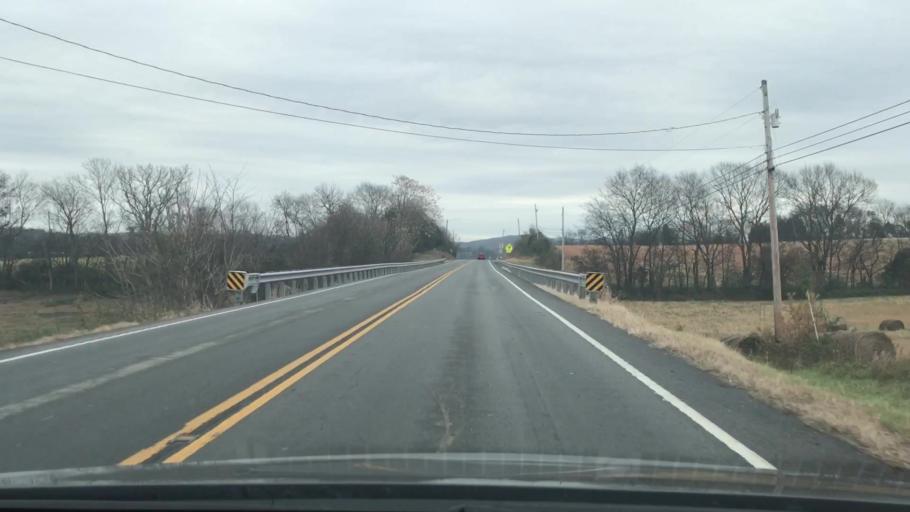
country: US
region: Tennessee
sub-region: Trousdale County
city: Hartsville
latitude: 36.4039
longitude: -86.1844
